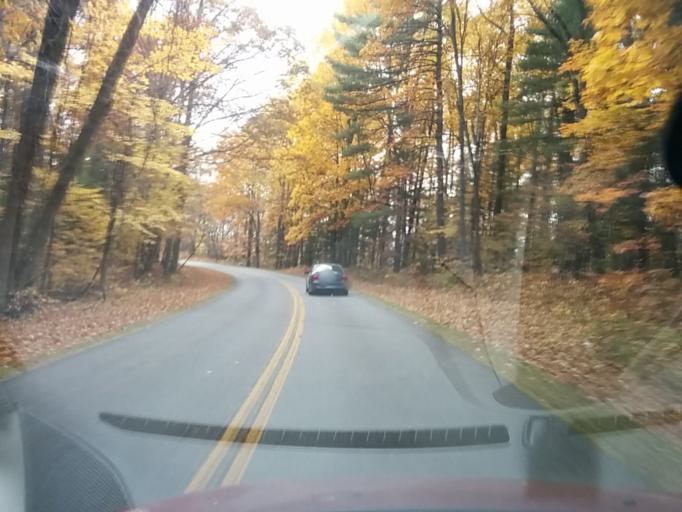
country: US
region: Virginia
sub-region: City of Buena Vista
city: Buena Vista
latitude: 37.8123
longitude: -79.2322
